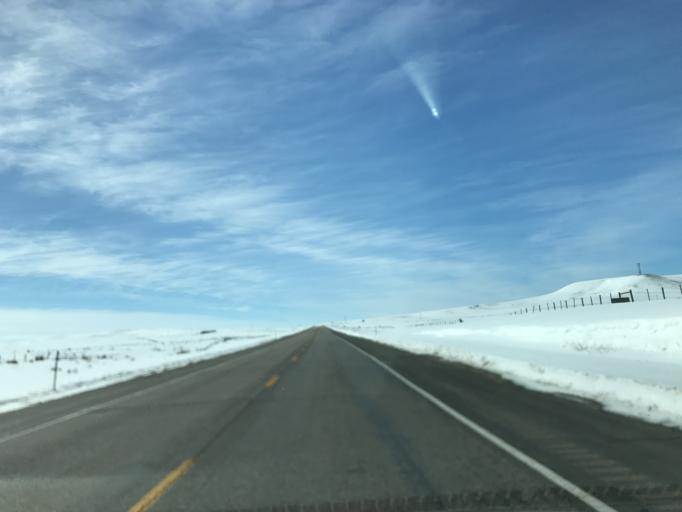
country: US
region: Wyoming
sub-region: Sublette County
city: Marbleton
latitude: 42.7320
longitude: -110.0747
